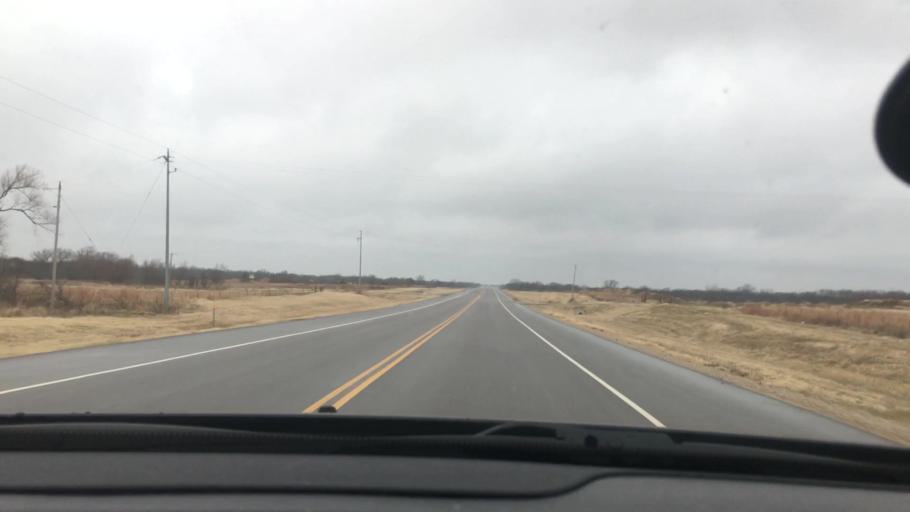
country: US
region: Oklahoma
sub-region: Johnston County
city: Tishomingo
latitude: 34.3409
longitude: -96.6435
